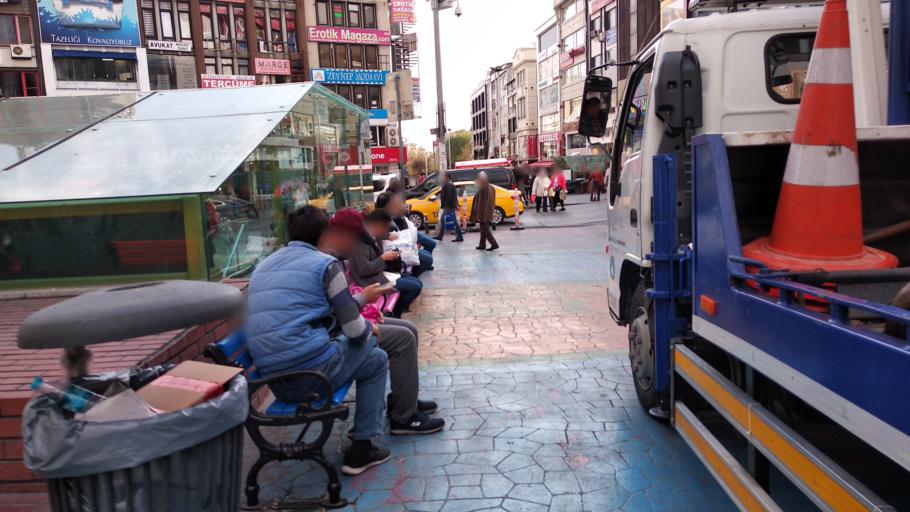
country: TR
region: Istanbul
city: Bahcelievler
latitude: 40.9788
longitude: 28.8744
